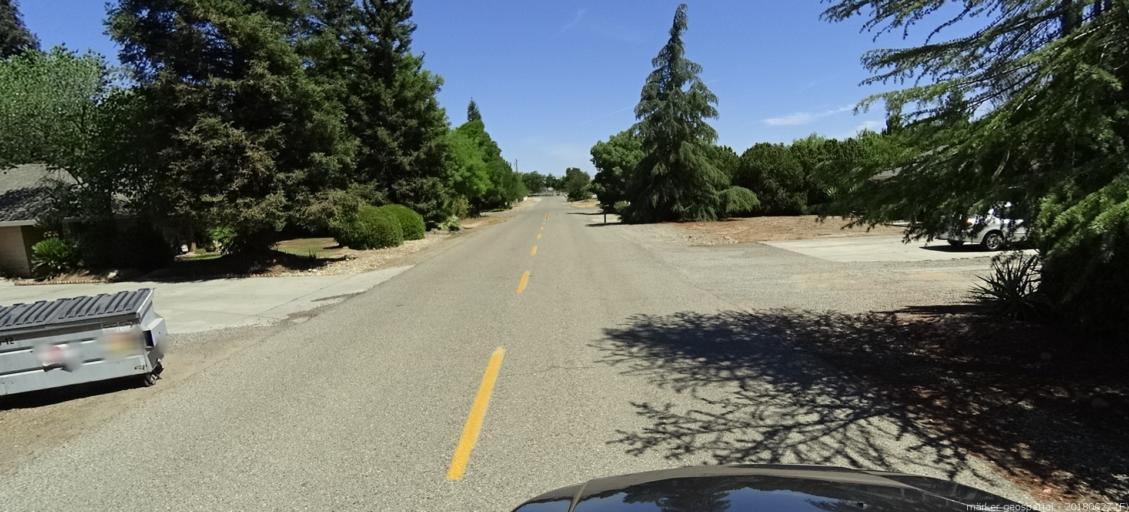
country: US
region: California
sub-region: Madera County
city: Bonadelle Ranchos-Madera Ranchos
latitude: 36.9277
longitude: -119.8882
